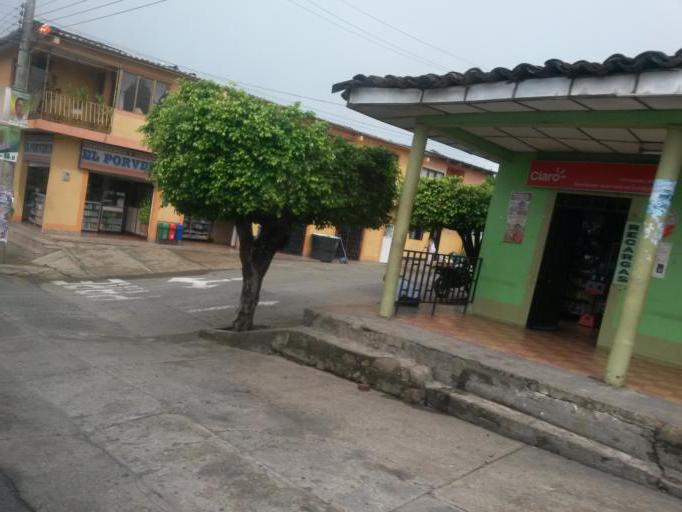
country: CO
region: Cauca
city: El Bordo
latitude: 2.1707
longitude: -76.8980
